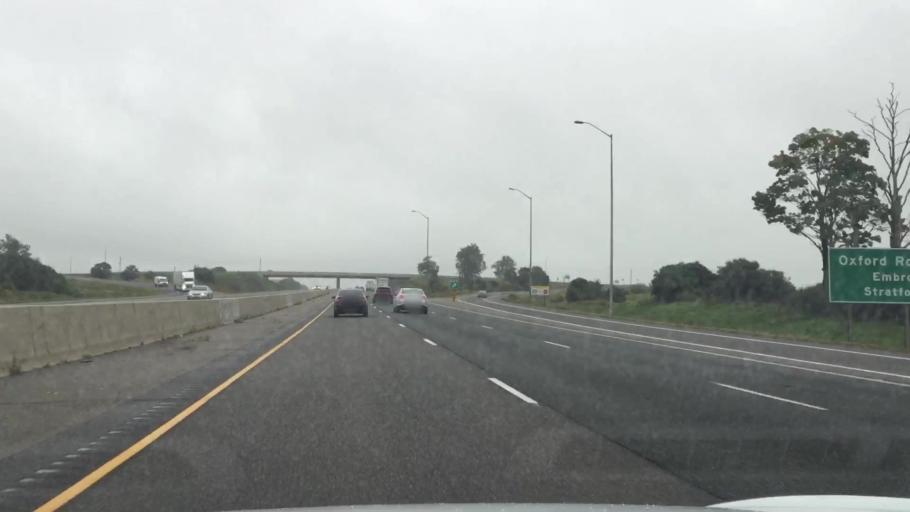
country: CA
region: Ontario
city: Ingersoll
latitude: 43.0490
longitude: -80.8262
